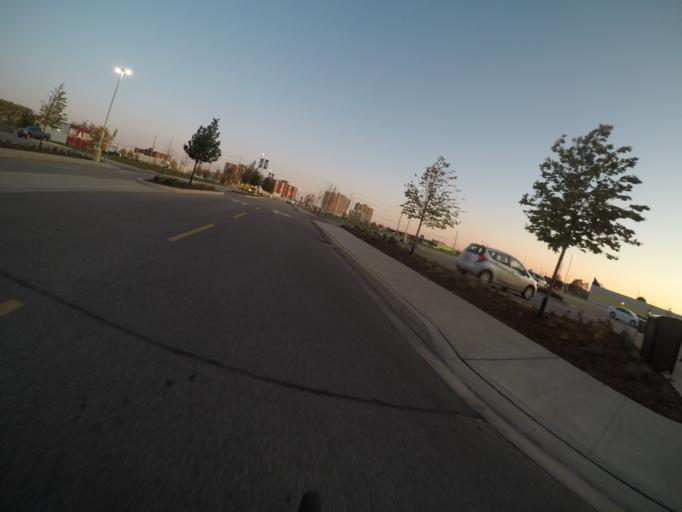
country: CA
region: Ontario
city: Kitchener
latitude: 43.4204
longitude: -80.4392
